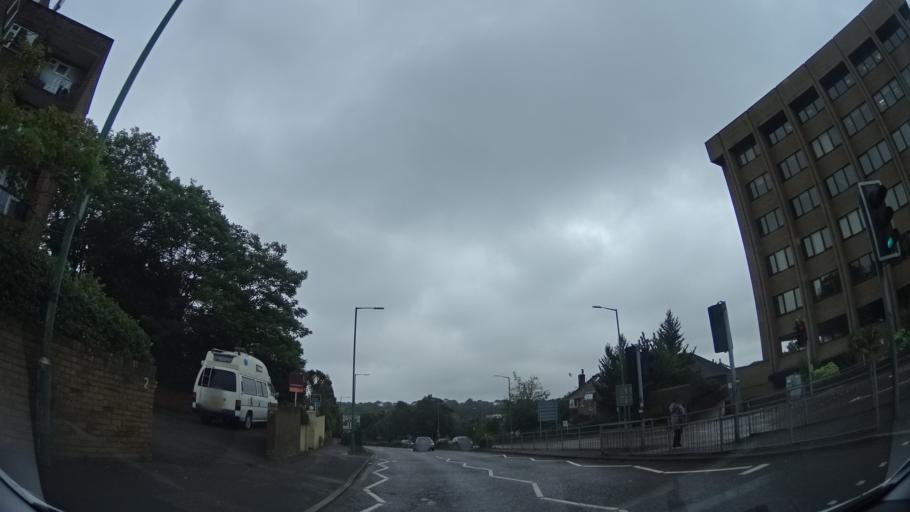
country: GB
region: England
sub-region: Bournemouth
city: Bournemouth
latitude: 50.7205
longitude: -1.8903
